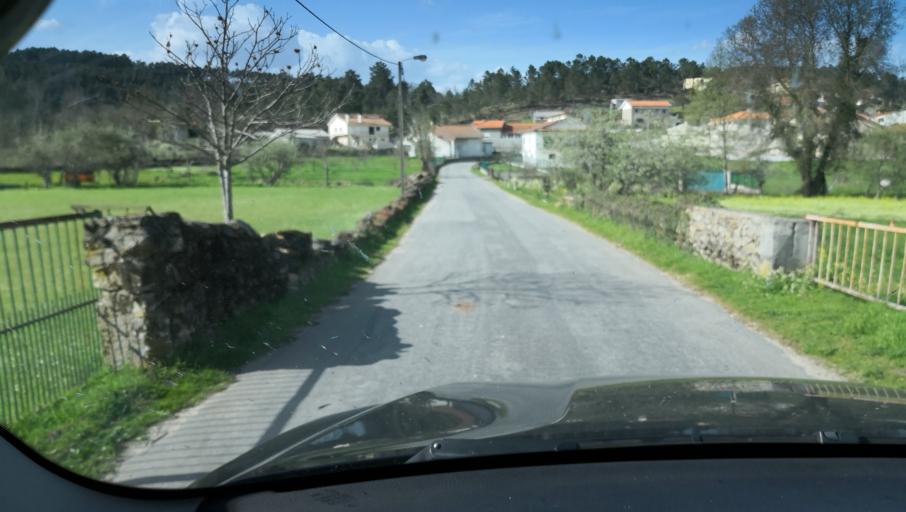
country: PT
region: Vila Real
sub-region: Vila Real
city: Vila Real
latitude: 41.2821
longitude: -7.6689
